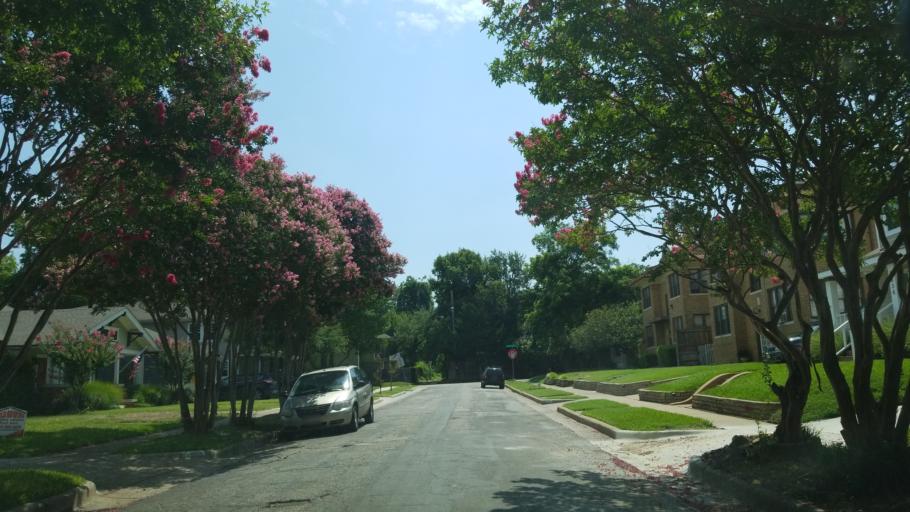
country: US
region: Texas
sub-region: Dallas County
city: Highland Park
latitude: 32.8192
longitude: -96.7710
